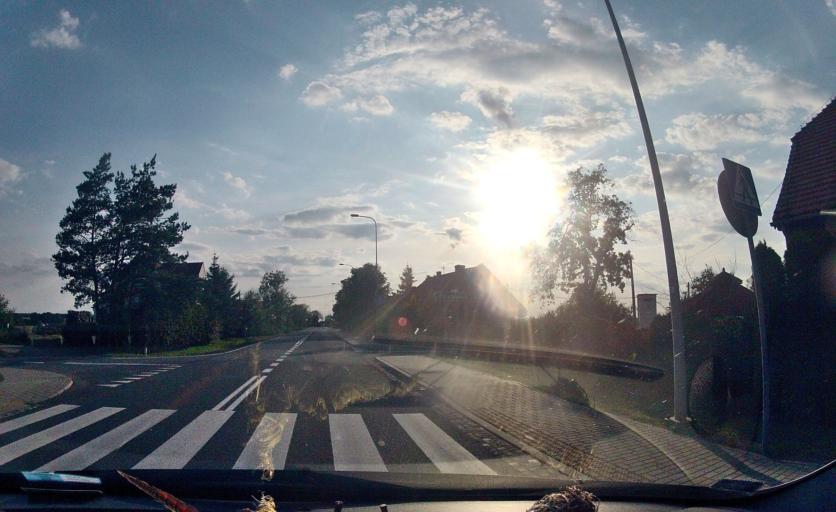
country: PL
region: Opole Voivodeship
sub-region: Powiat oleski
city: Gorzow Slaski
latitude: 51.0108
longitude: 18.3698
